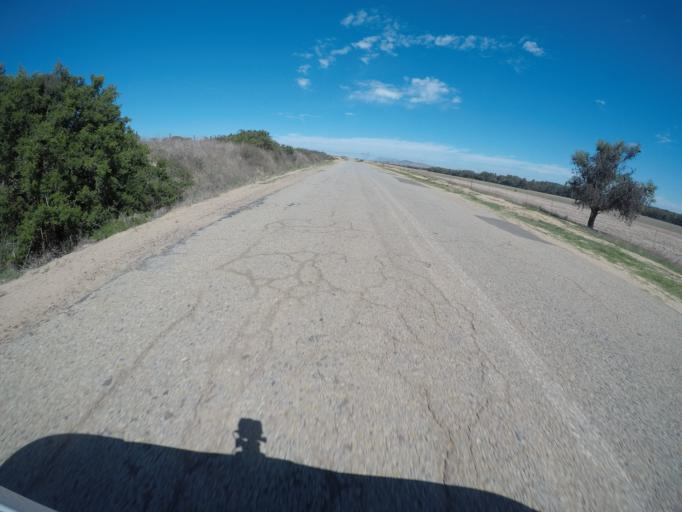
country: ZA
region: Western Cape
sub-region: West Coast District Municipality
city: Malmesbury
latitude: -33.5906
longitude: 18.6458
